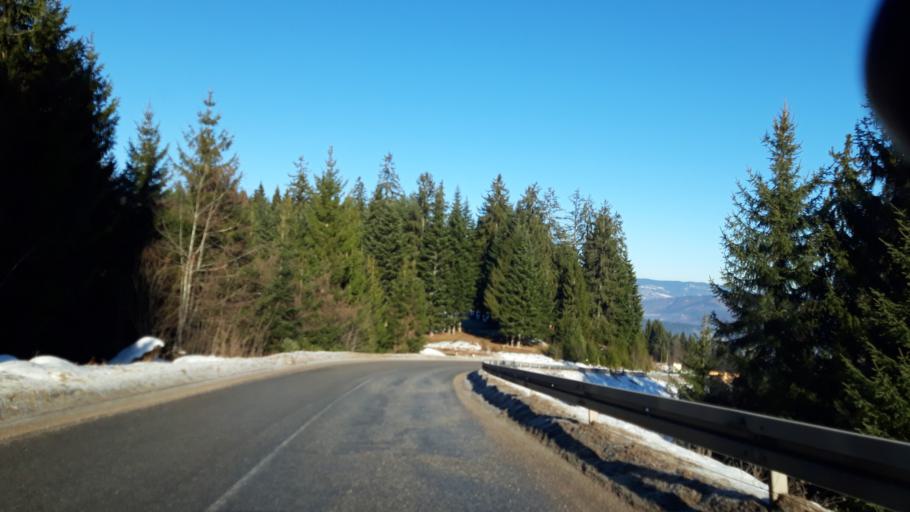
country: BA
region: Republika Srpska
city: Koran
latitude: 43.7914
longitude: 18.5558
